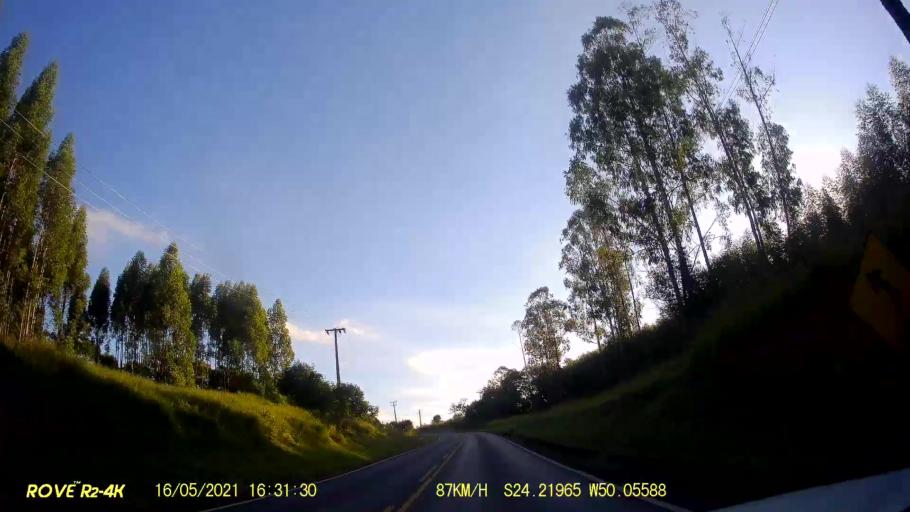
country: BR
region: Parana
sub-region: Pirai Do Sul
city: Pirai do Sul
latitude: -24.2197
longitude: -50.0560
